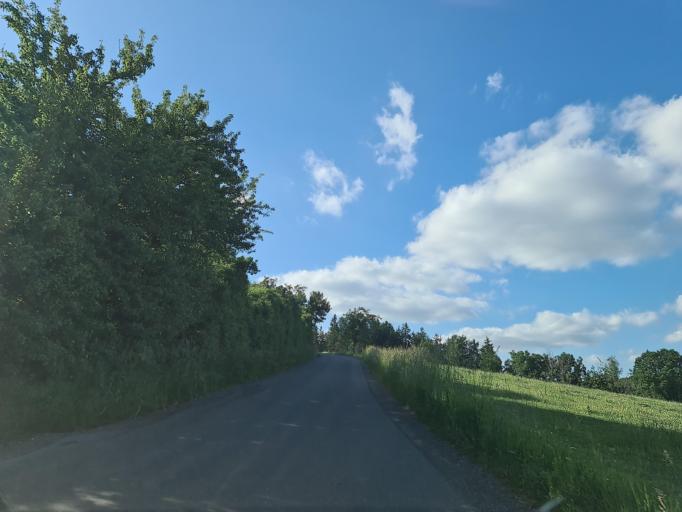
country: DE
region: Saxony
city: Mehltheuer
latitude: 50.5003
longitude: 12.0296
